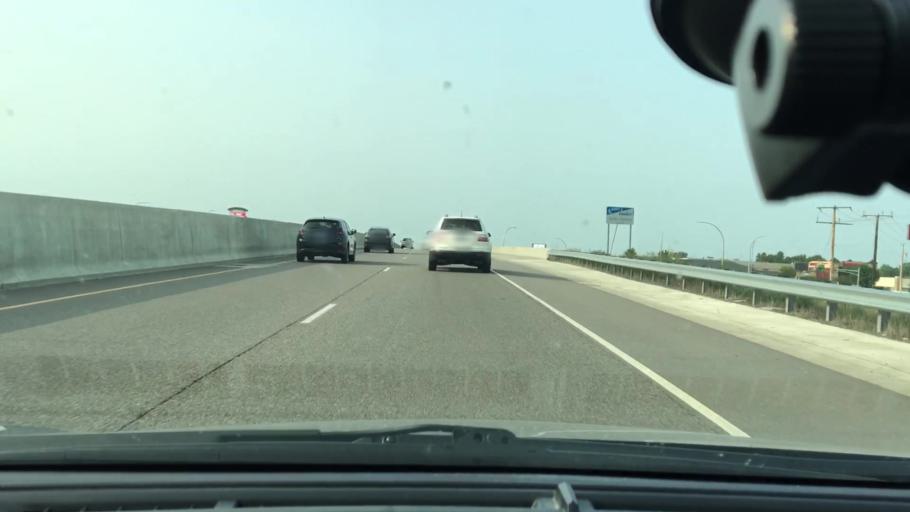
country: US
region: Minnesota
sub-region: Hennepin County
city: Rogers
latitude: 45.2088
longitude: -93.5525
